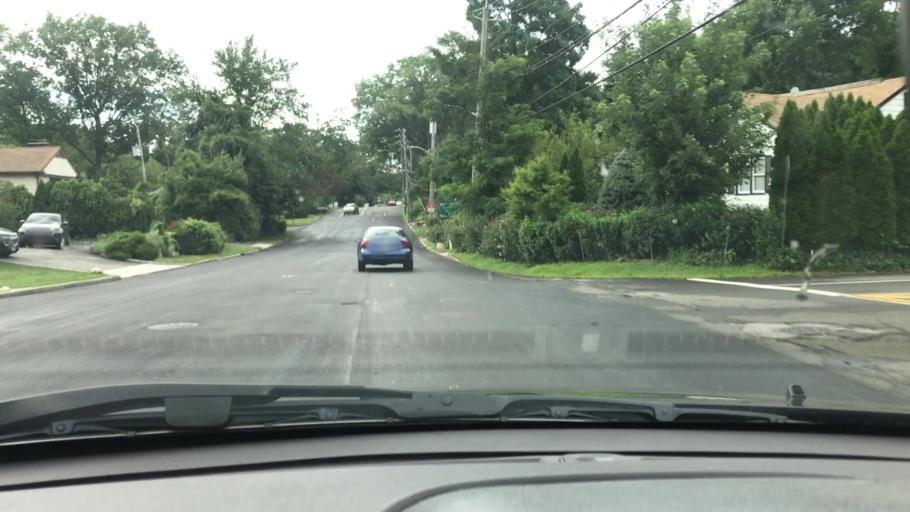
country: US
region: New York
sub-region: Westchester County
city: Tuckahoe
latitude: 40.9417
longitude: -73.7993
